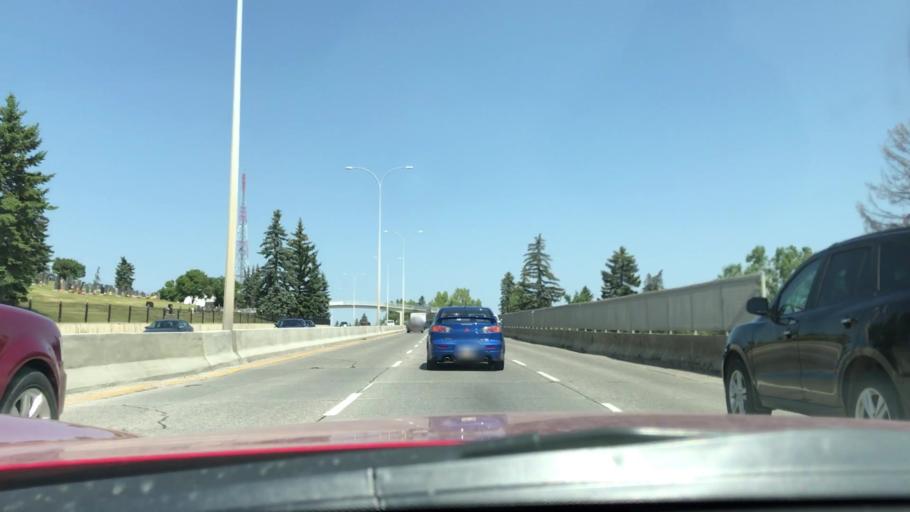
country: CA
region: Alberta
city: Calgary
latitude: 51.0237
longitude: -114.0592
